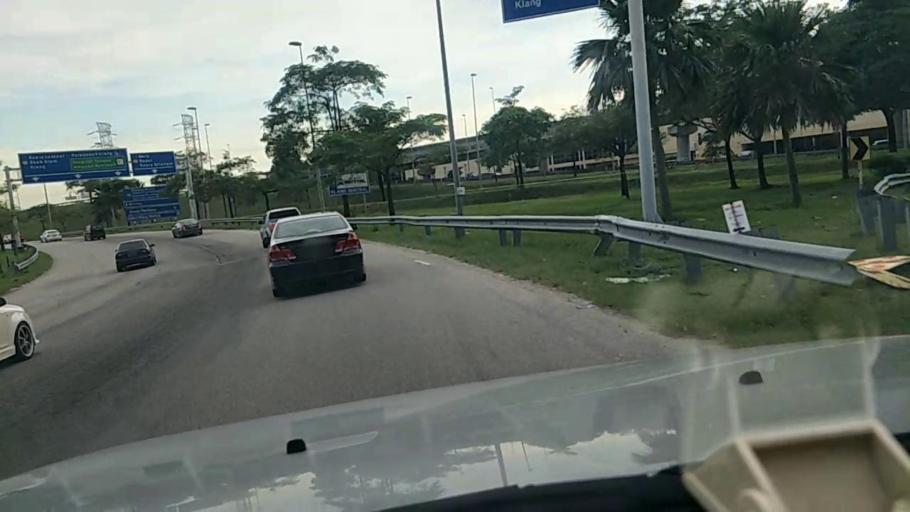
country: MY
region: Selangor
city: Klang
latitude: 3.1090
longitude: 101.4430
